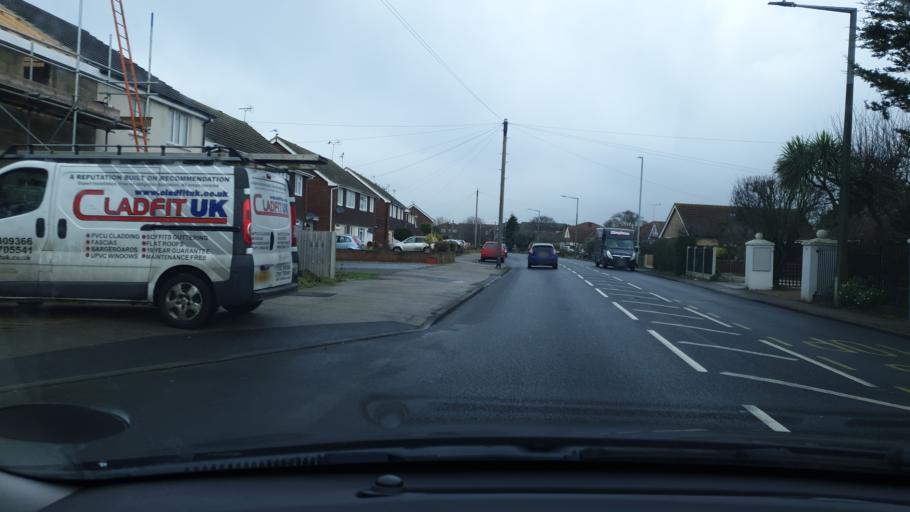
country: GB
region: England
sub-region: Essex
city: Clacton-on-Sea
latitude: 51.8005
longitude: 1.1306
